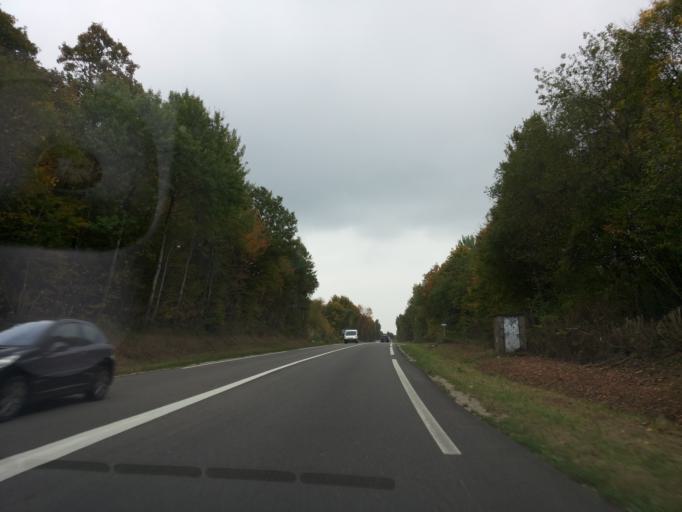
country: FR
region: Alsace
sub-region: Departement du Bas-Rhin
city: Saverne
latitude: 48.7667
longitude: 7.3180
